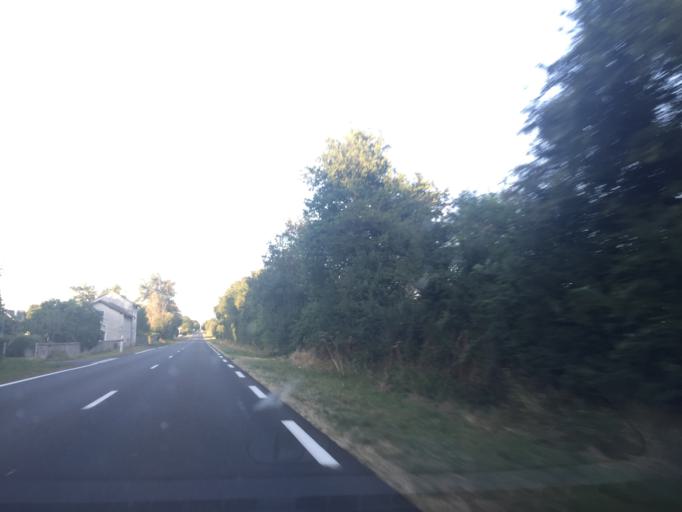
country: FR
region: Poitou-Charentes
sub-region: Departement de la Vienne
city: Rouille
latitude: 46.3960
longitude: 0.0649
